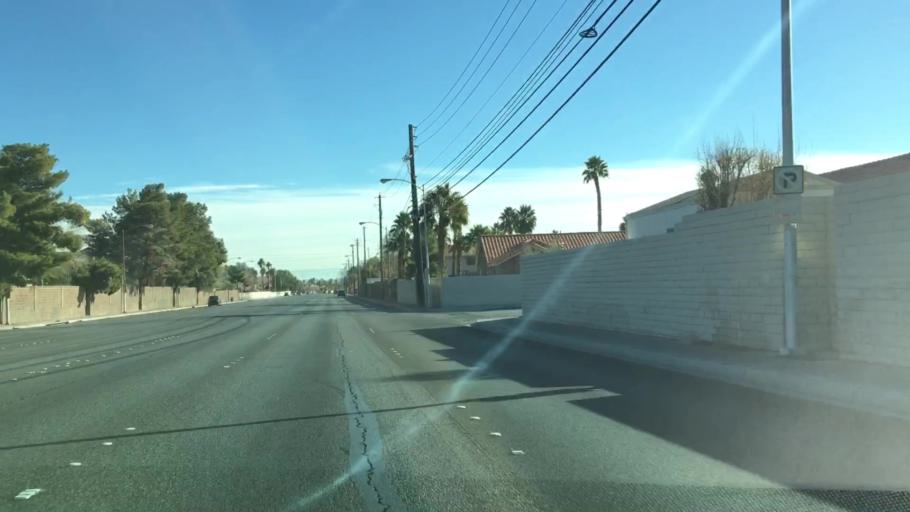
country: US
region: Nevada
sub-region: Clark County
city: Paradise
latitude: 36.0574
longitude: -115.1347
